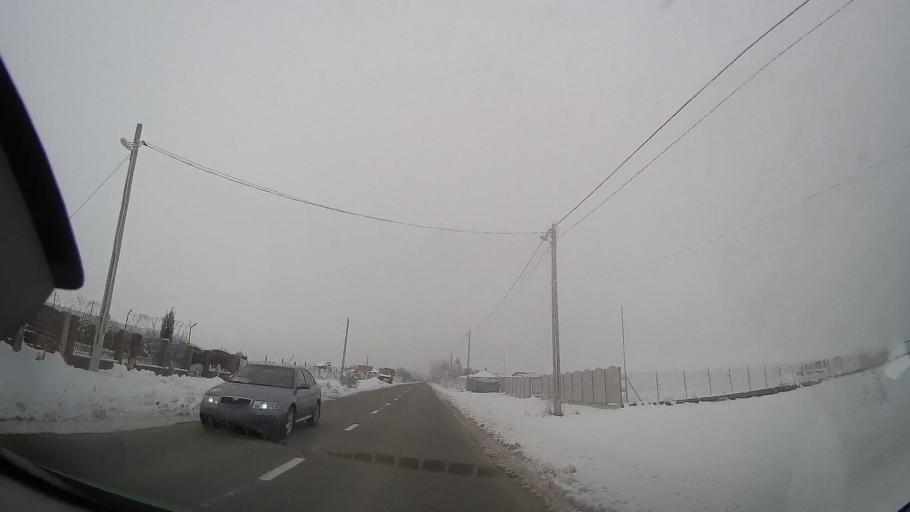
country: RO
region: Neamt
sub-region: Comuna Horia
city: Cotu Vames
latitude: 46.8948
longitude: 26.9610
